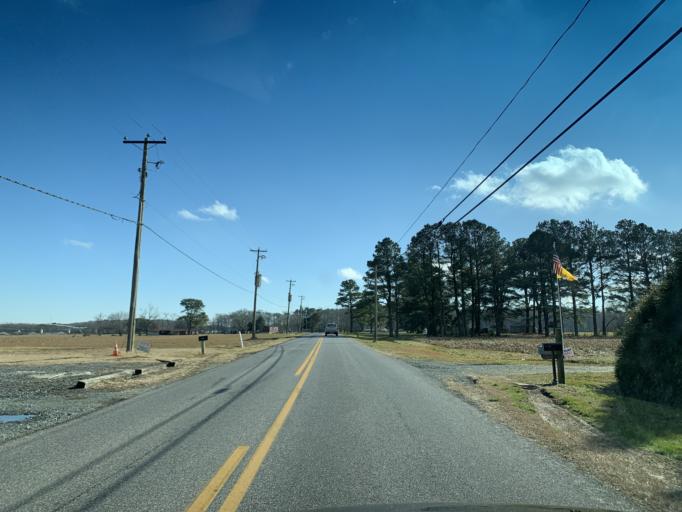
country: US
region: Delaware
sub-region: Sussex County
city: Selbyville
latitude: 38.4365
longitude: -75.1869
